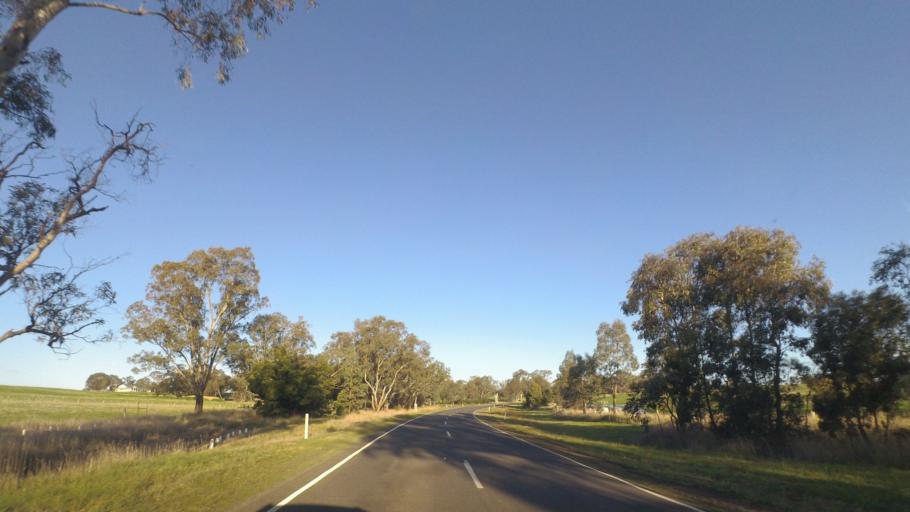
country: AU
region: Victoria
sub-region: Mount Alexander
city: Castlemaine
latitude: -37.0958
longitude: 144.5109
